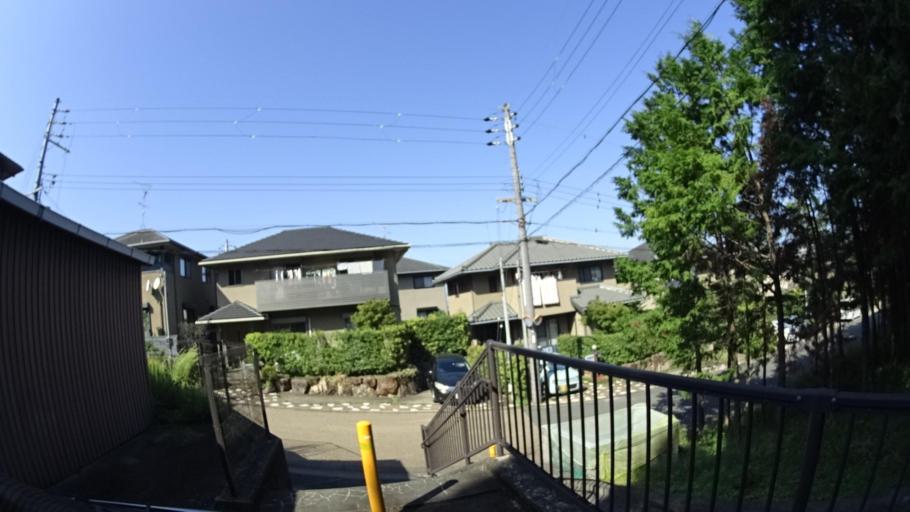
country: JP
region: Kyoto
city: Tanabe
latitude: 34.8213
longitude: 135.7565
